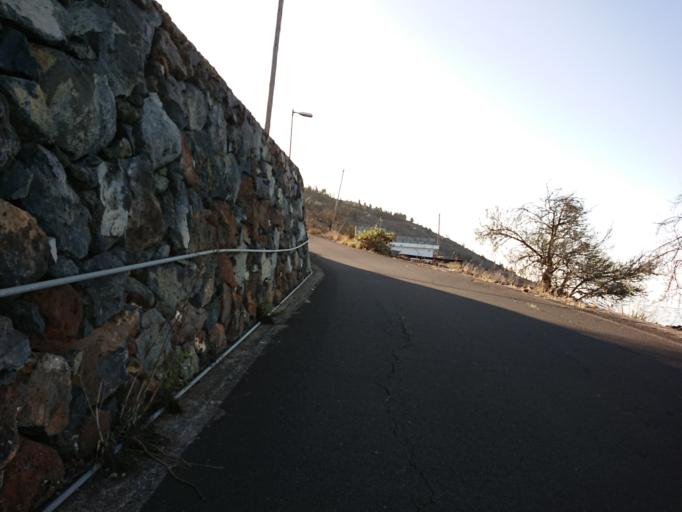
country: ES
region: Canary Islands
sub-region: Provincia de Santa Cruz de Tenerife
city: Tijarafe
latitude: 28.6804
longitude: -17.9414
